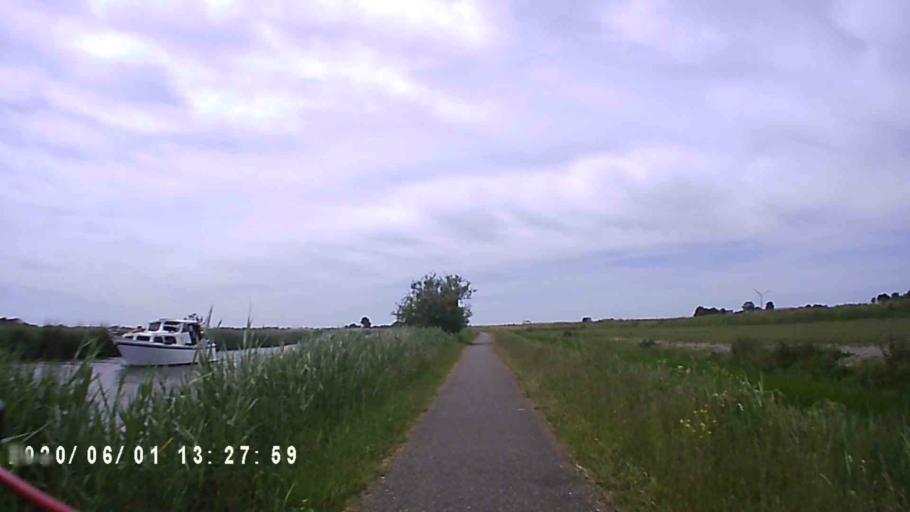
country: NL
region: Friesland
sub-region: Gemeente Littenseradiel
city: Wommels
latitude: 53.1035
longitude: 5.5758
